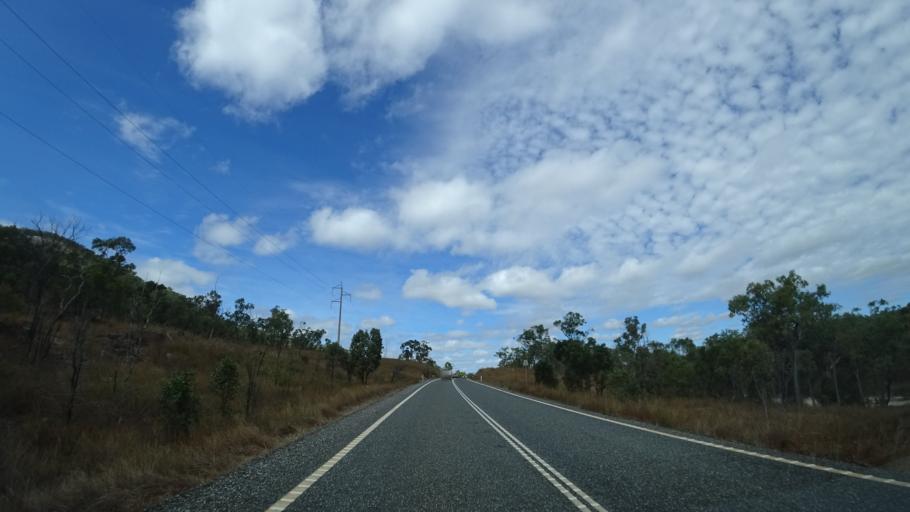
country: AU
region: Queensland
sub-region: Cairns
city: Port Douglas
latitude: -16.3399
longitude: 144.7257
